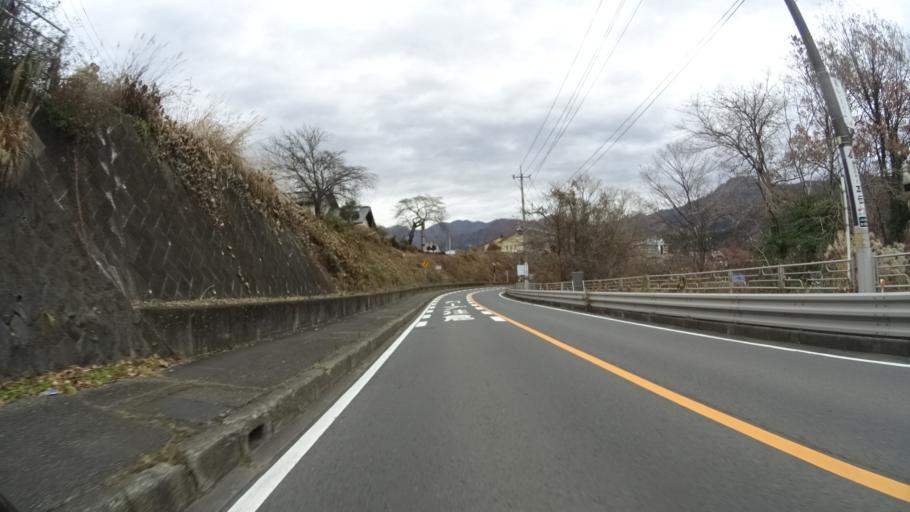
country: JP
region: Gunma
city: Nakanojomachi
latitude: 36.7269
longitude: 138.8890
